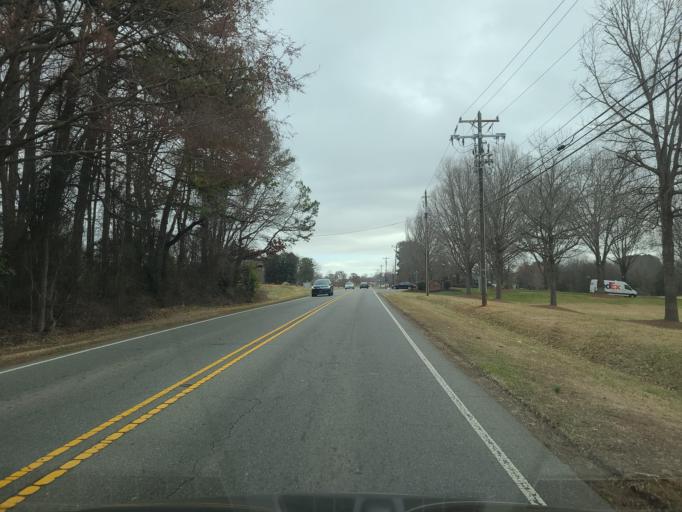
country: US
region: North Carolina
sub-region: Mecklenburg County
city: Mint Hill
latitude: 35.1893
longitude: -80.6961
